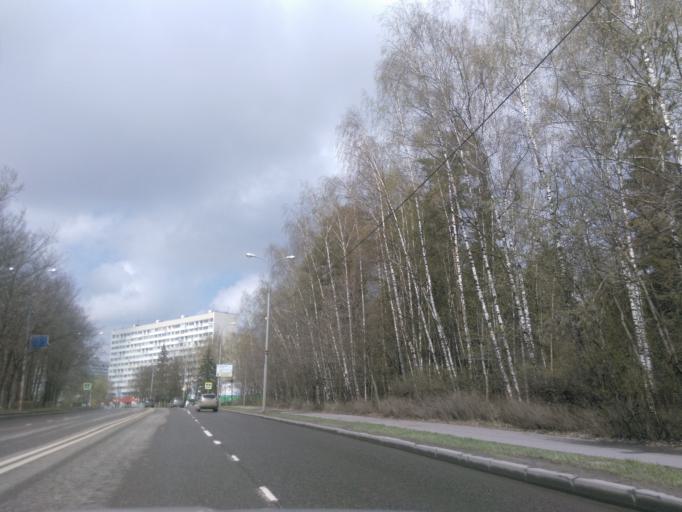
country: RU
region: Moskovskaya
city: Rzhavki
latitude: 55.9865
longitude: 37.2358
